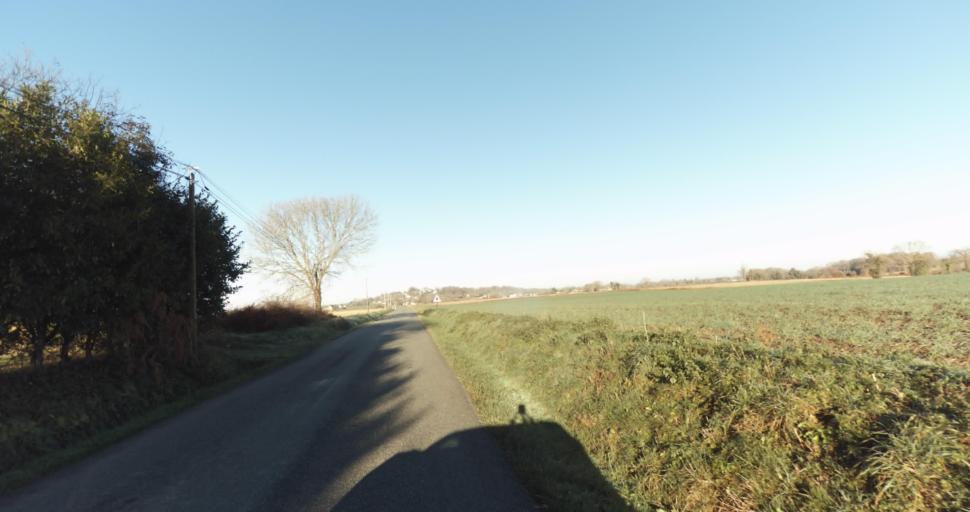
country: FR
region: Aquitaine
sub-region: Departement des Pyrenees-Atlantiques
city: Morlaas
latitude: 43.3172
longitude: -0.2413
